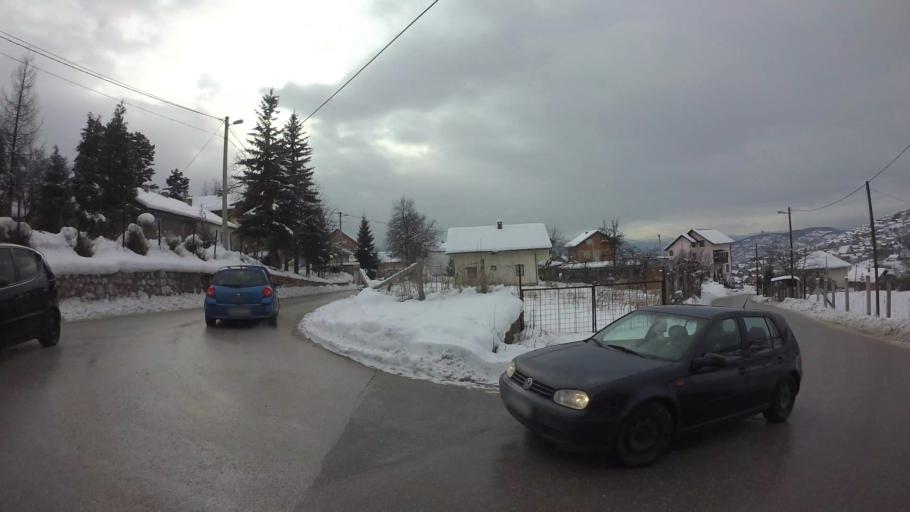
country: BA
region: Federation of Bosnia and Herzegovina
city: Kobilja Glava
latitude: 43.8722
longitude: 18.4420
